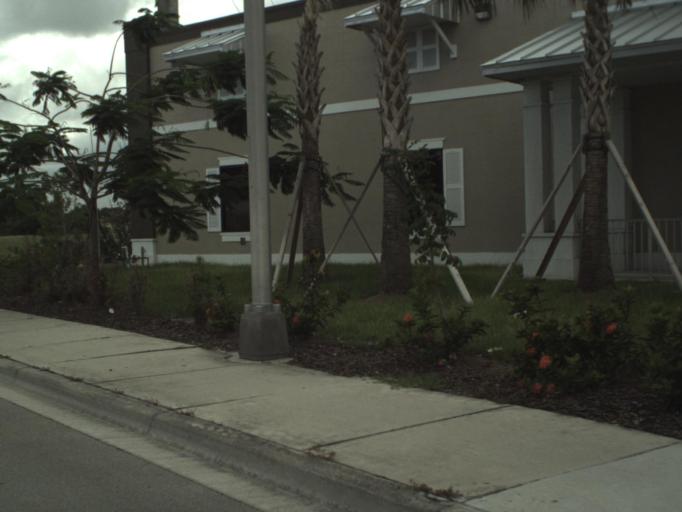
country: US
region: Florida
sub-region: Broward County
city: Pompano Beach Highlands
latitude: 26.3000
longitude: -80.1068
